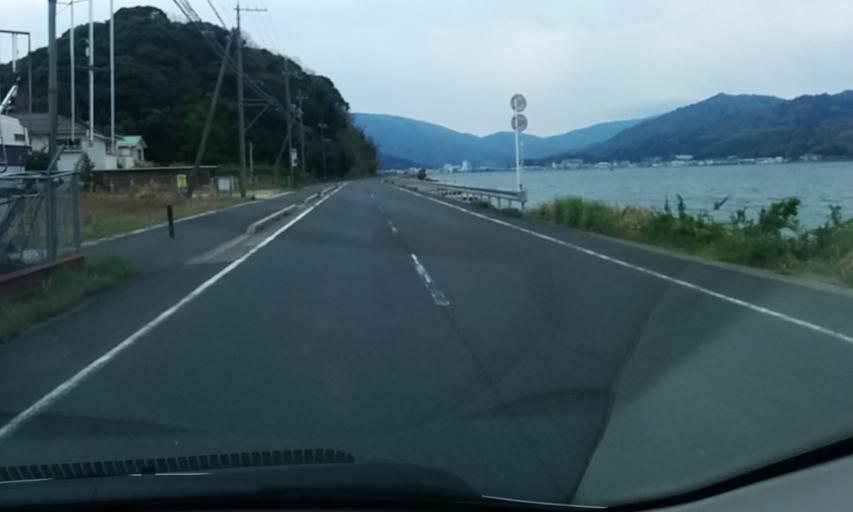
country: JP
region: Kyoto
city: Miyazu
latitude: 35.5586
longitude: 135.2047
